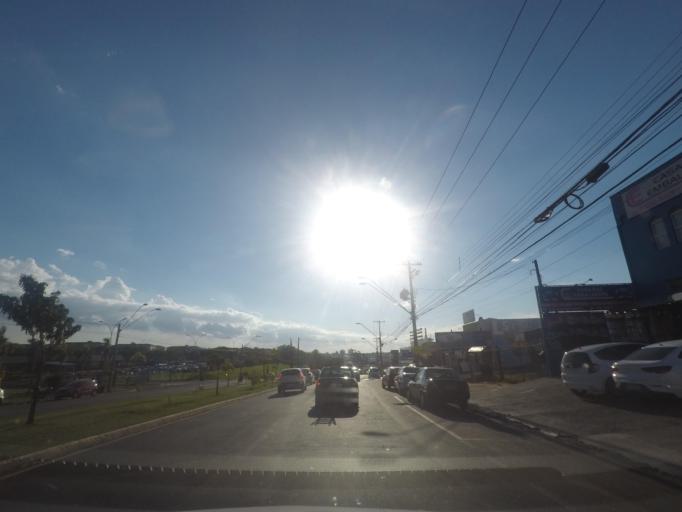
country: BR
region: Sao Paulo
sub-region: Sumare
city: Sumare
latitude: -22.8178
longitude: -47.2476
